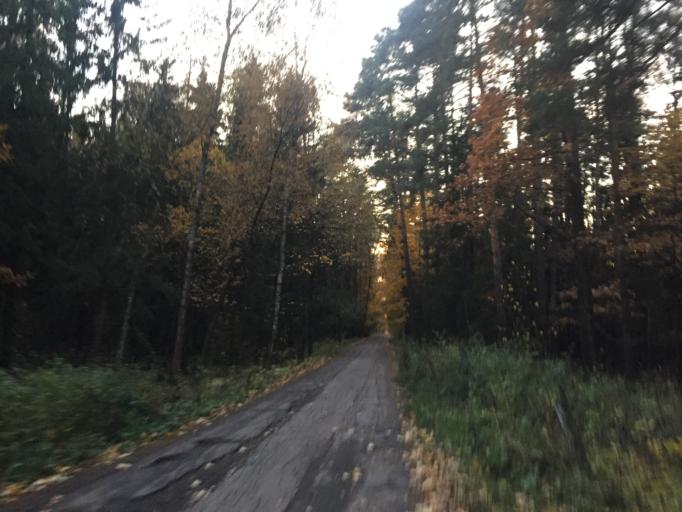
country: RU
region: Moskovskaya
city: Druzhba
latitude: 55.8626
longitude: 37.7767
